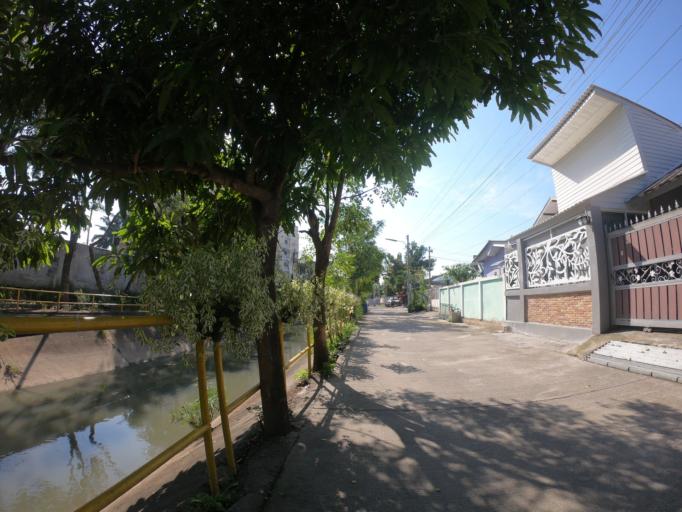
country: TH
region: Chiang Mai
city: Chiang Mai
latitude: 18.7989
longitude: 98.9939
